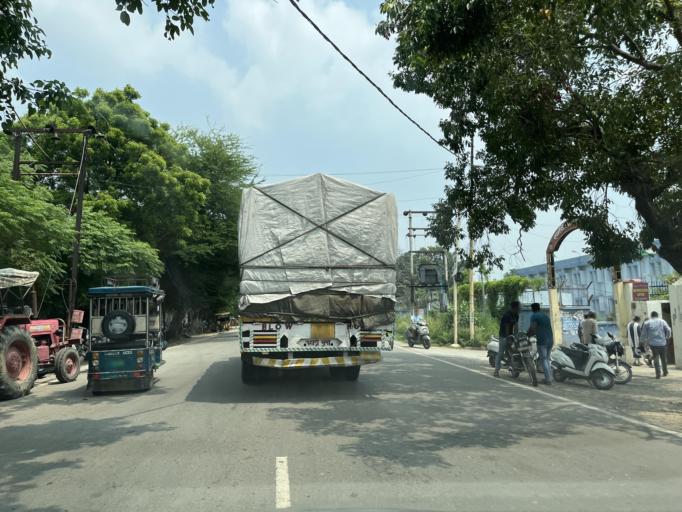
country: IN
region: Uttar Pradesh
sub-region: Bijnor
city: Najibabad
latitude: 29.6001
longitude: 78.3401
